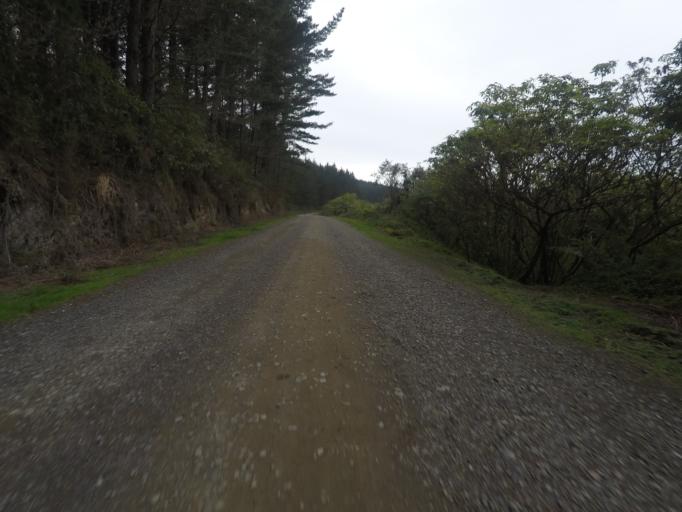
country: NZ
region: Auckland
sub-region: Auckland
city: Muriwai Beach
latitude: -36.7511
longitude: 174.5752
